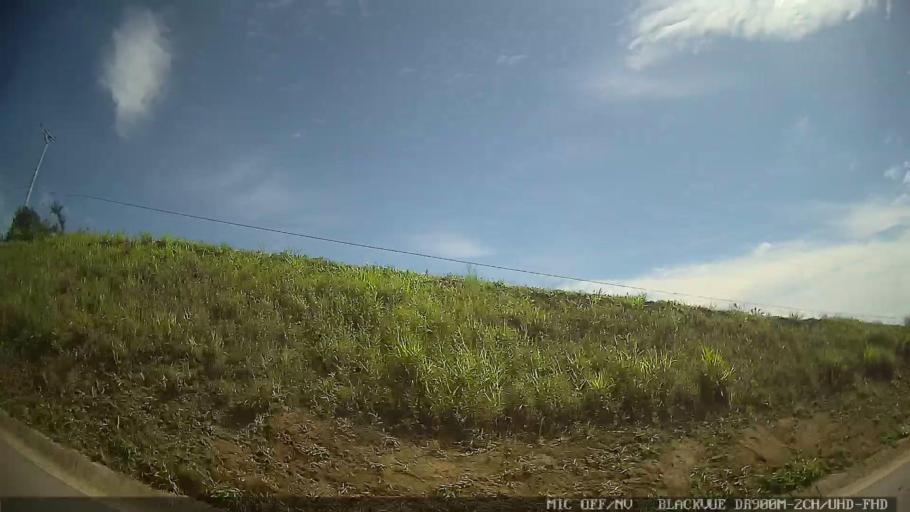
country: BR
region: Sao Paulo
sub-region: Porto Feliz
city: Porto Feliz
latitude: -23.2103
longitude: -47.5925
